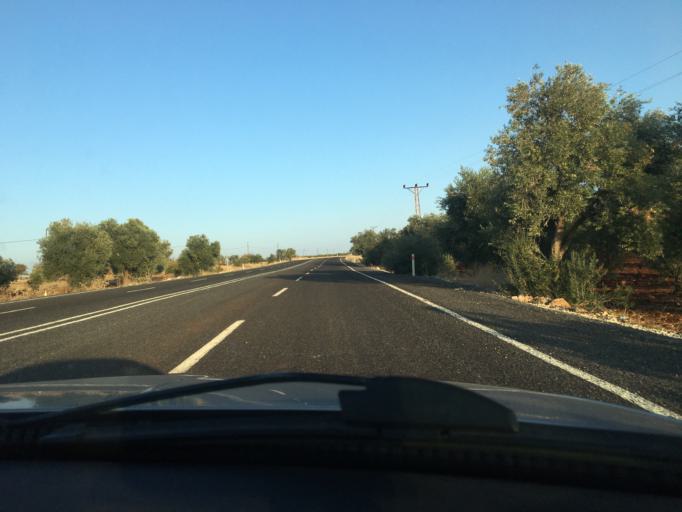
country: TR
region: Sanliurfa
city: Halfeti
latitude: 37.2439
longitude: 37.8922
